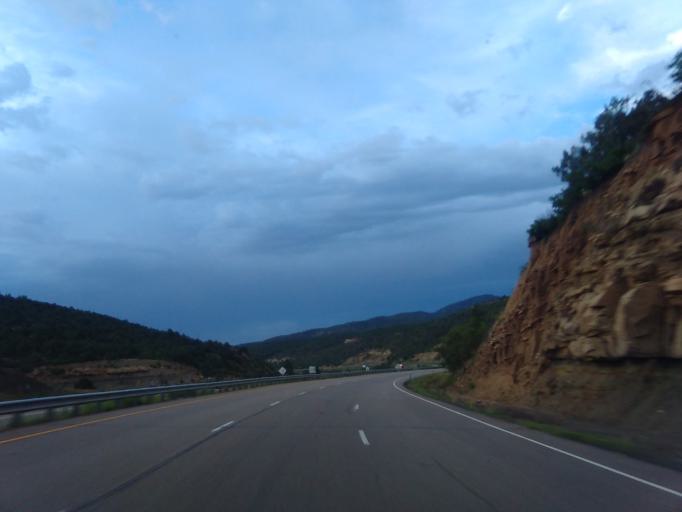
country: US
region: Colorado
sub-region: Las Animas County
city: Trinidad
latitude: 37.0611
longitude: -104.5230
